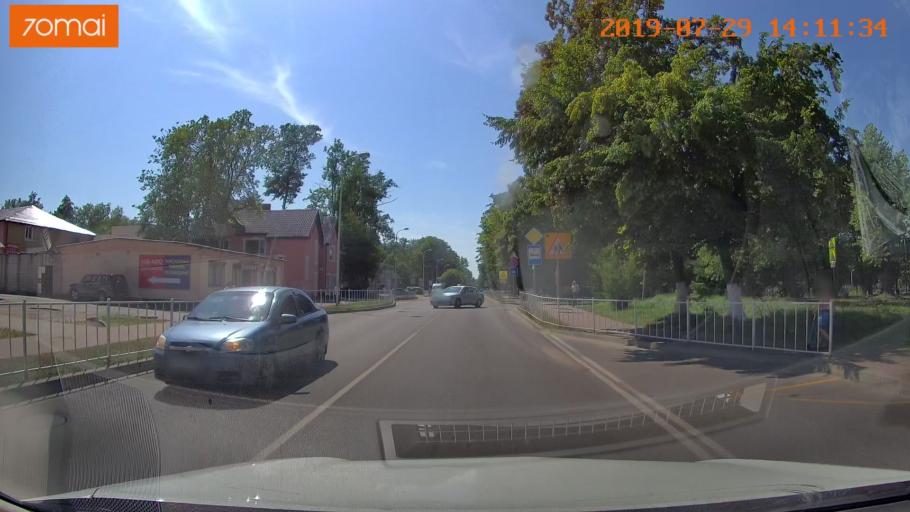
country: RU
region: Kaliningrad
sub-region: Gorod Kaliningrad
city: Baltiysk
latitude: 54.6513
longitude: 19.9071
